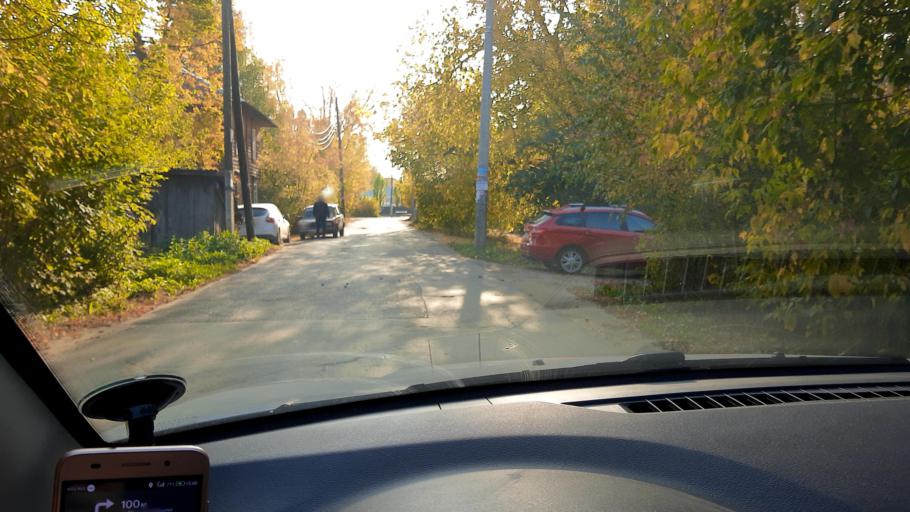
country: RU
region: Nizjnij Novgorod
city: Nizhniy Novgorod
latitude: 56.2663
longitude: 43.9314
